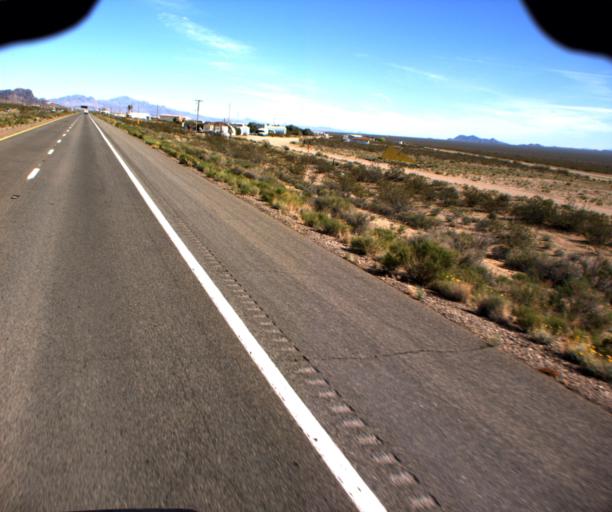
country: US
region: Arizona
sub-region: Mohave County
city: Dolan Springs
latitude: 35.7093
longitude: -114.4794
